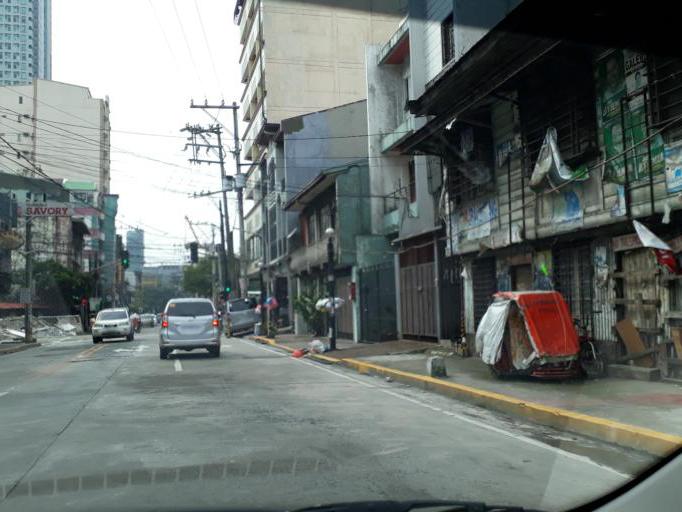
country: PH
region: Metro Manila
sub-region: City of Manila
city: Manila
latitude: 14.6065
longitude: 120.9937
